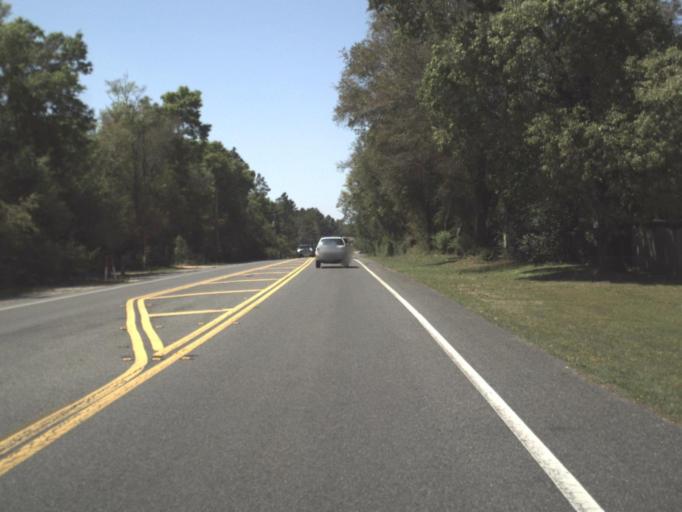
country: US
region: Florida
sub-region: Escambia County
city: Bellview
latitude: 30.4903
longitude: -87.3204
